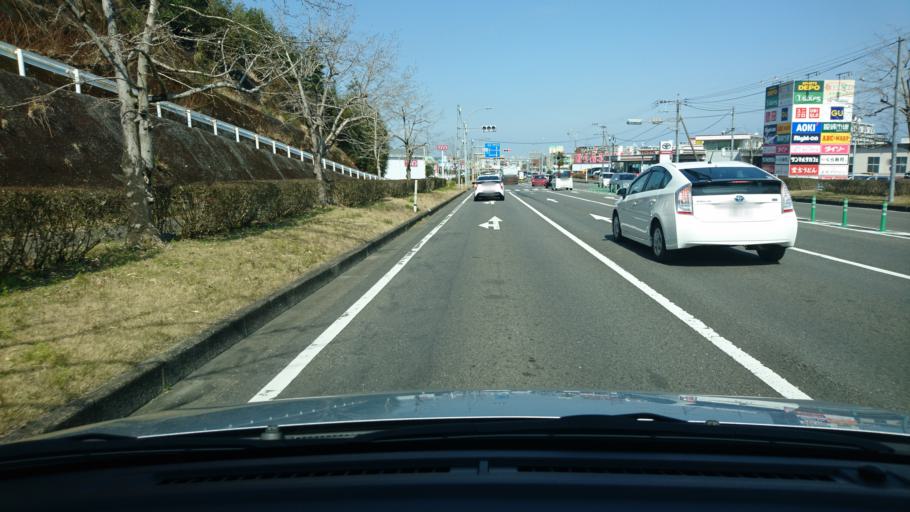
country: JP
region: Miyazaki
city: Miyazaki-shi
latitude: 31.8856
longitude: 131.4117
